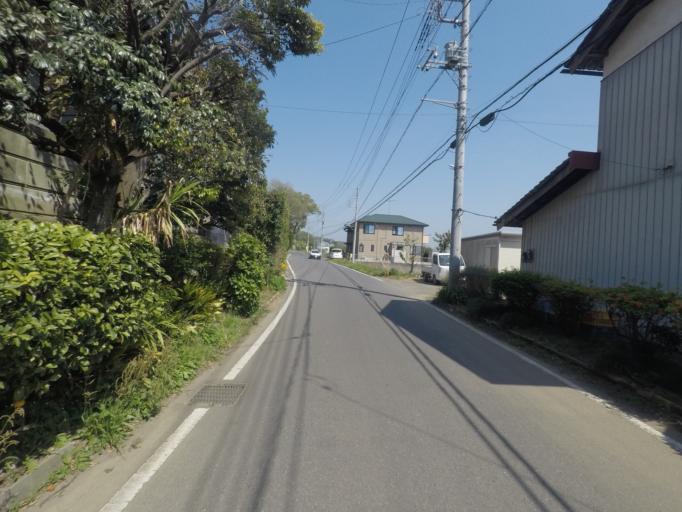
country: JP
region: Ibaraki
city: Ami
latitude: 36.0737
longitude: 140.2673
